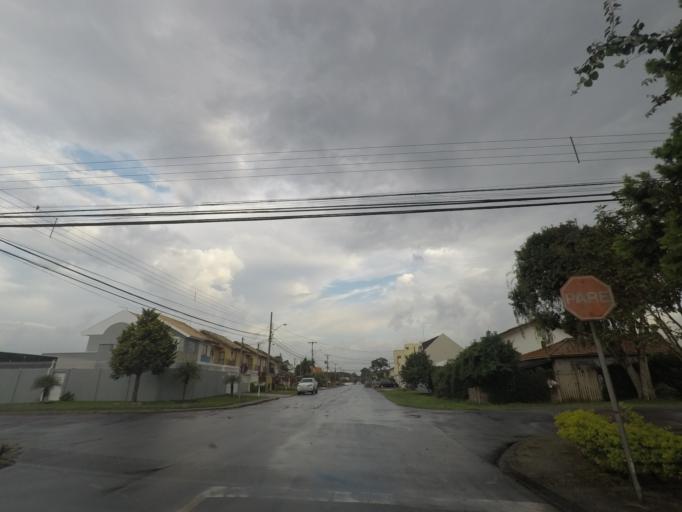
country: BR
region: Parana
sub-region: Sao Jose Dos Pinhais
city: Sao Jose dos Pinhais
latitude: -25.4901
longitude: -49.2486
